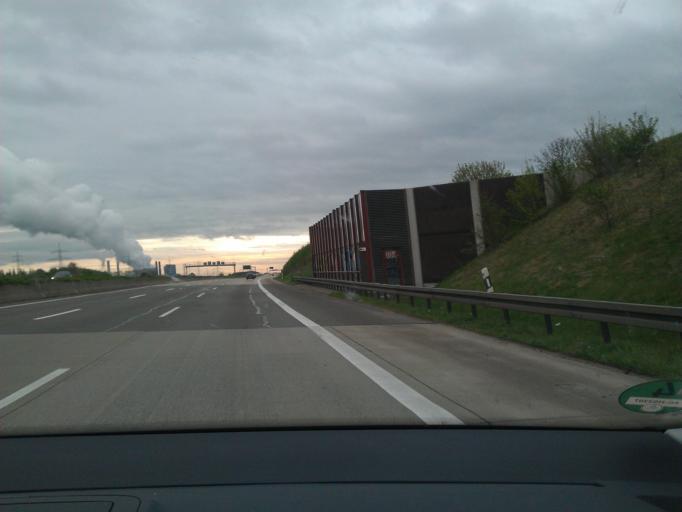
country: DE
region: North Rhine-Westphalia
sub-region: Regierungsbezirk Koln
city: Eschweiler
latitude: 50.8265
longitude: 6.2549
